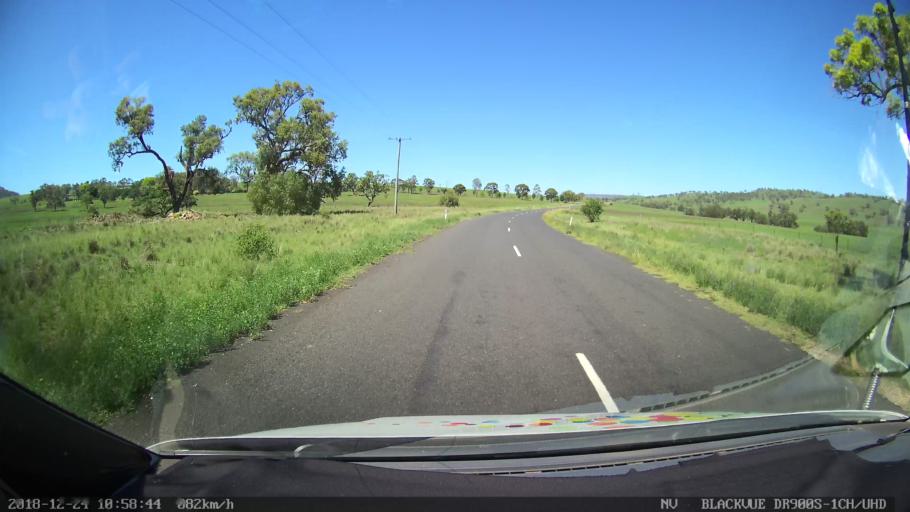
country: AU
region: New South Wales
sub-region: Upper Hunter Shire
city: Merriwa
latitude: -32.0508
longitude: 150.4049
